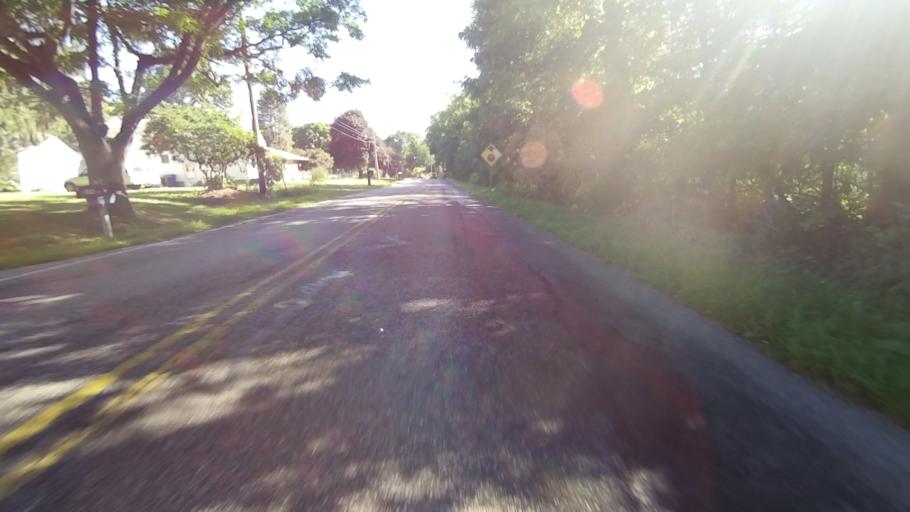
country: US
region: Ohio
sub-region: Portage County
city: Kent
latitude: 41.1421
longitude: -81.3795
